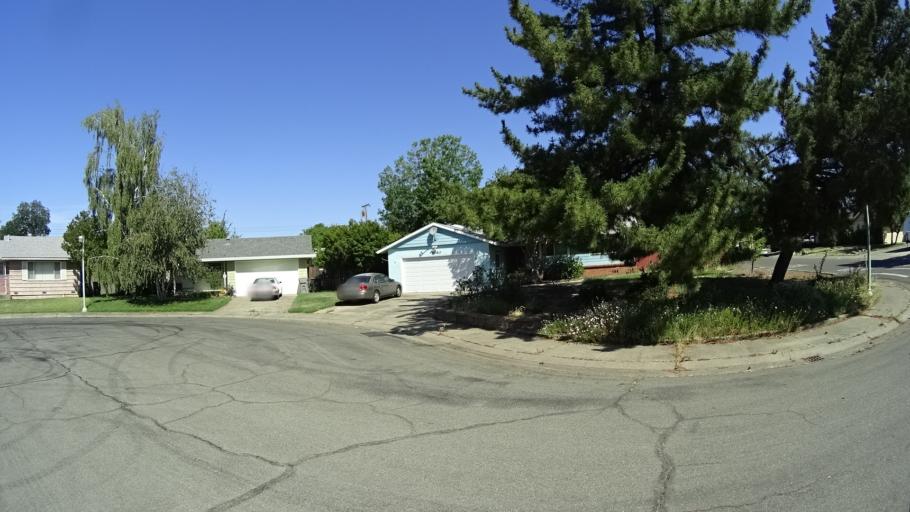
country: US
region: California
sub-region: Sacramento County
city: Parkway
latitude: 38.5290
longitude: -121.4521
